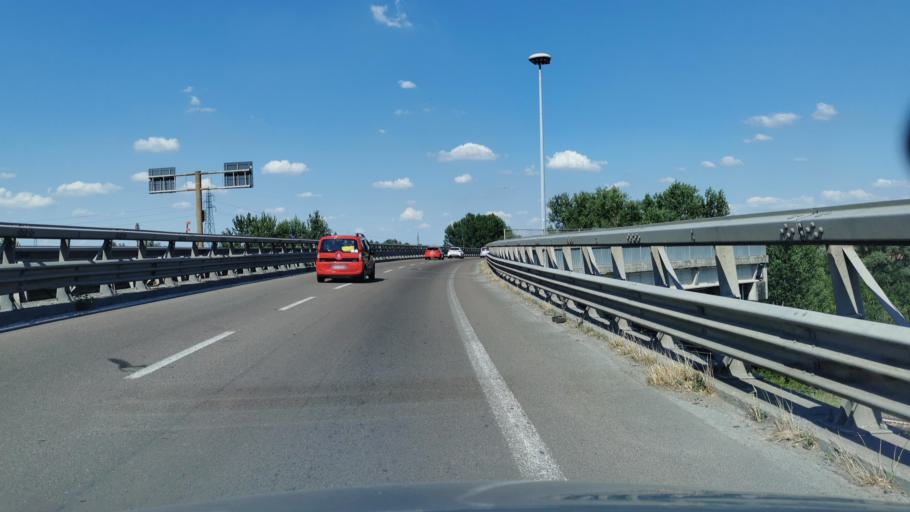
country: IT
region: Emilia-Romagna
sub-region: Provincia di Modena
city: Villanova
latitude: 44.6713
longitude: 10.9102
